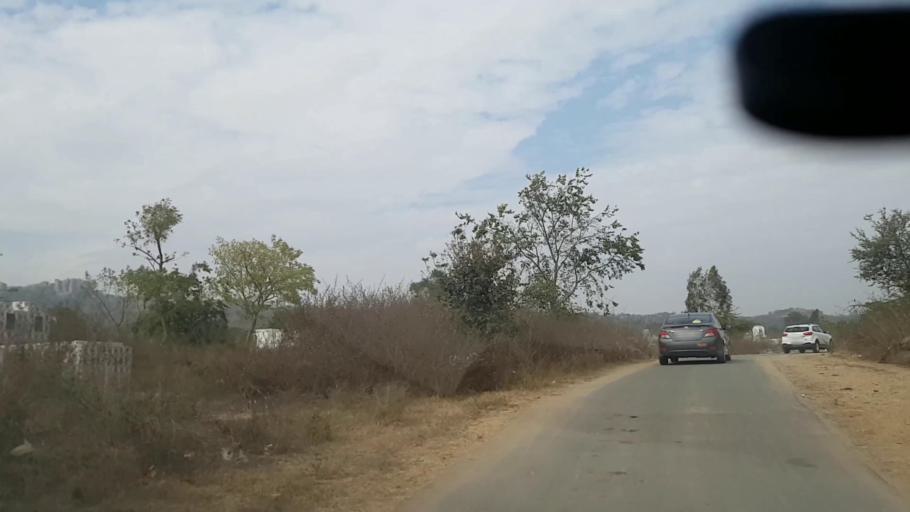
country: IN
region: Telangana
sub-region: Rangareddi
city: Lal Bahadur Nagar
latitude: 17.1631
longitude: 78.7866
